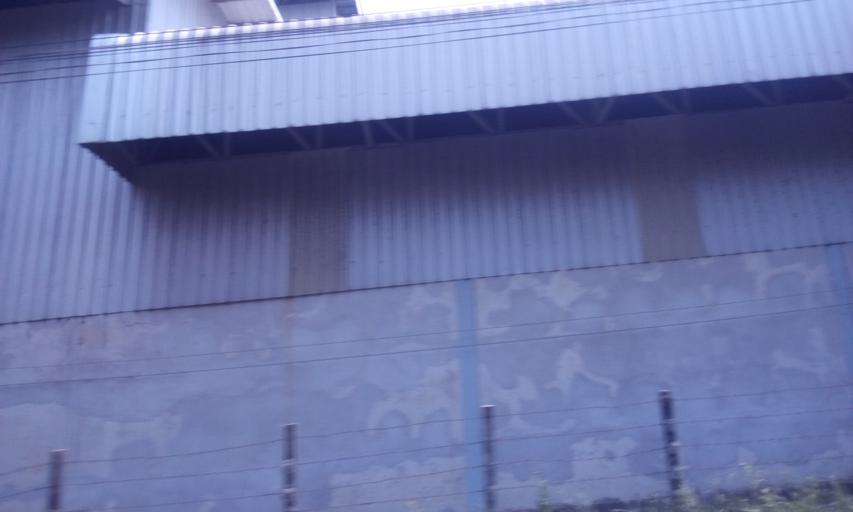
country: TH
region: Chachoengsao
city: Bang Nam Priao
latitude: 13.9699
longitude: 100.9663
